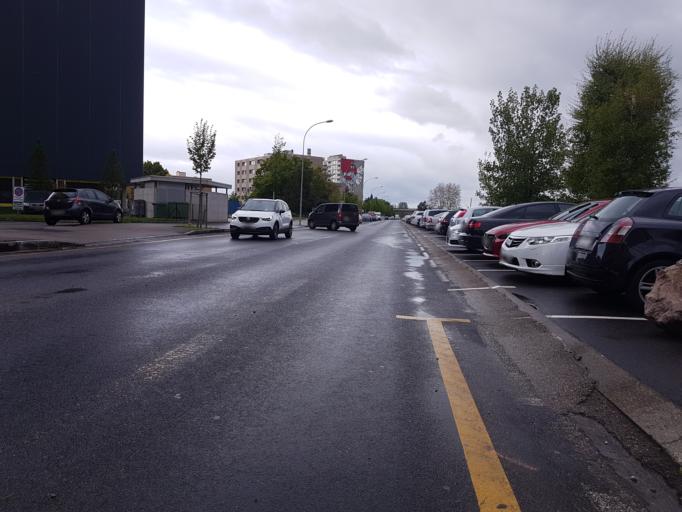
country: CH
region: Vaud
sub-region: Jura-Nord vaudois District
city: Yverdon-les-Bains
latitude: 46.7734
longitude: 6.6313
